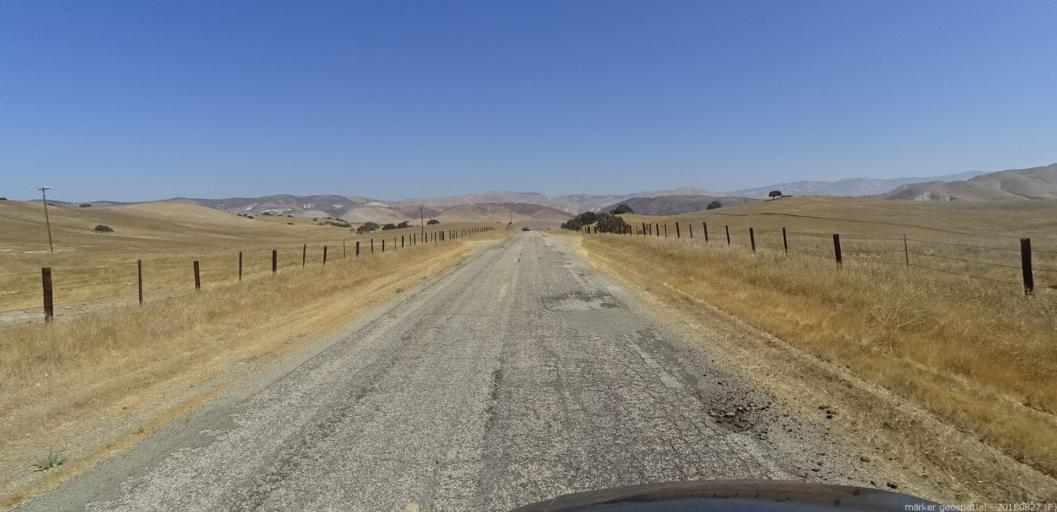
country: US
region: California
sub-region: Monterey County
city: King City
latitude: 36.2569
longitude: -120.9989
